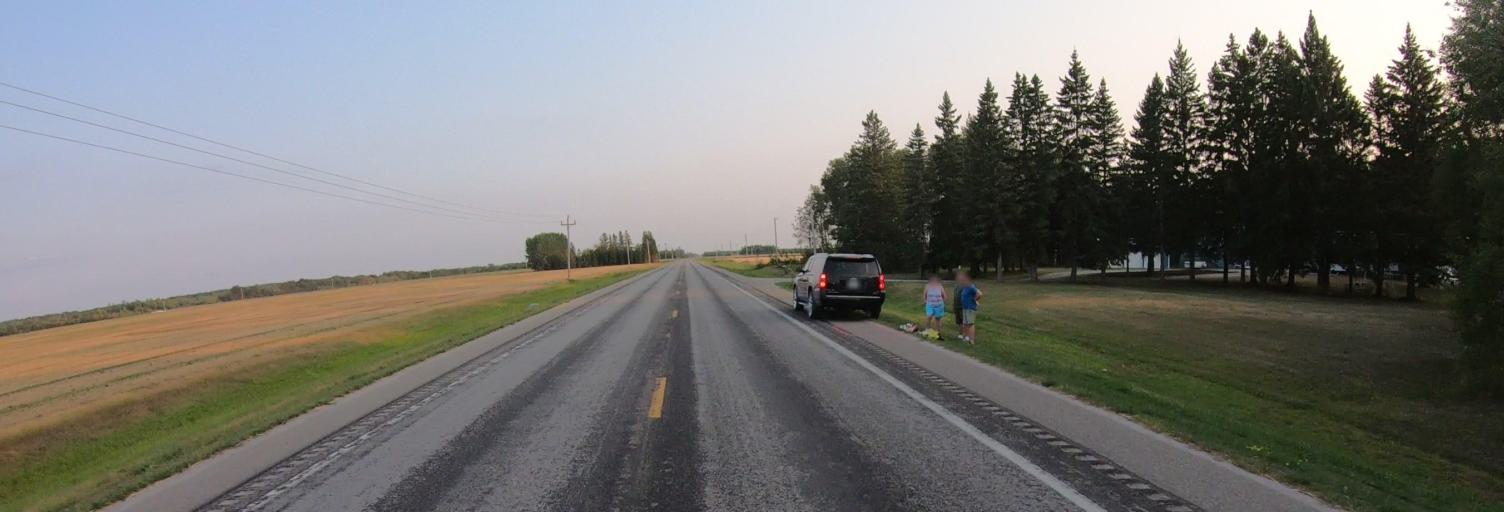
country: US
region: Minnesota
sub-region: Roseau County
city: Warroad
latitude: 48.8633
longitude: -95.3305
